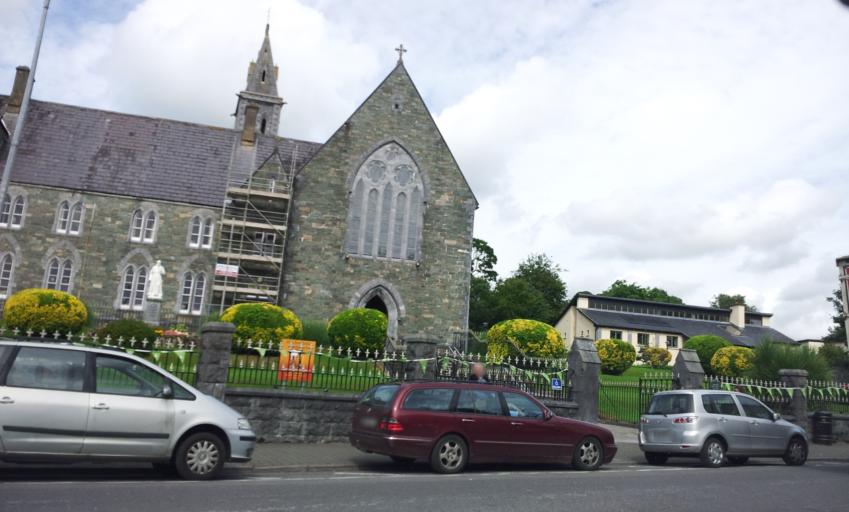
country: IE
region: Munster
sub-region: Ciarrai
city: Cill Airne
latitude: 52.0599
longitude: -9.5045
